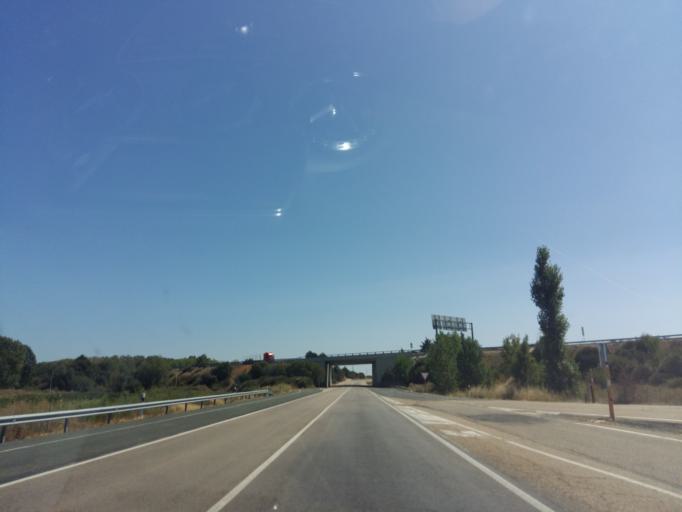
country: ES
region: Castille and Leon
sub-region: Provincia de Leon
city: San Justo de la Vega
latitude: 42.4400
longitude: -6.0376
